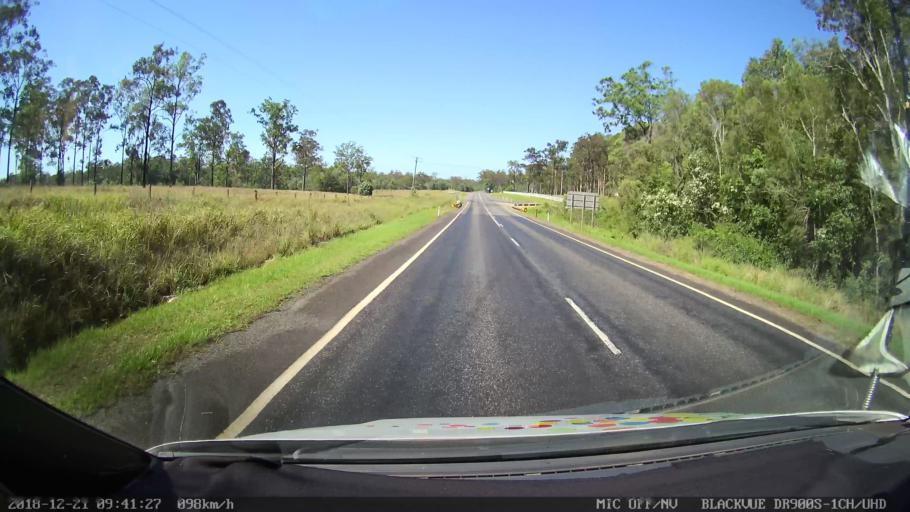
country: AU
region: New South Wales
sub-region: Clarence Valley
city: Grafton
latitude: -29.5853
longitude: 152.9570
